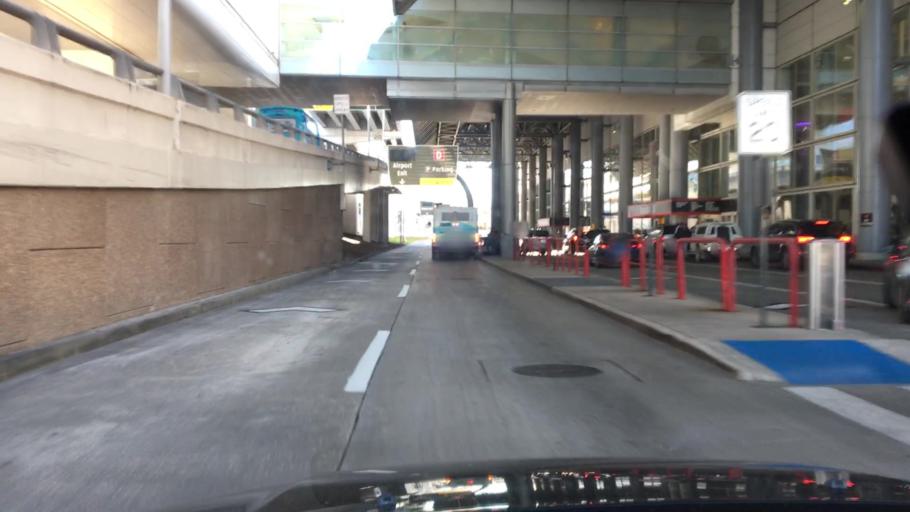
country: US
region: Texas
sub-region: Harris County
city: Humble
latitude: 29.9873
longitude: -95.3333
